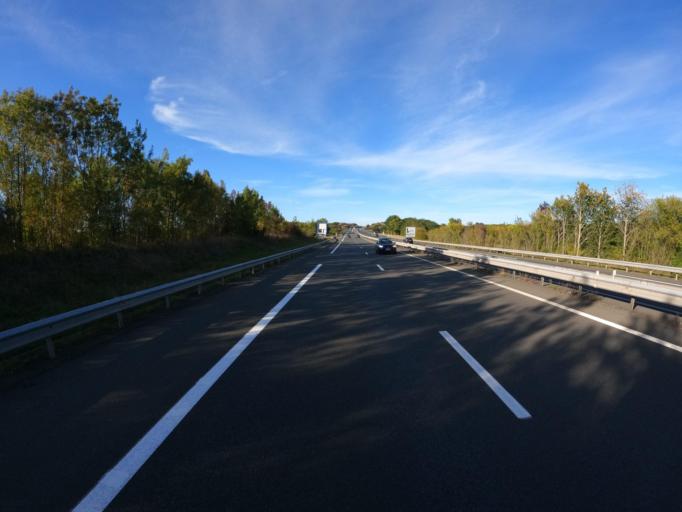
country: FR
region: Pays de la Loire
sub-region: Departement de Maine-et-Loire
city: Beaulieu-sur-Layon
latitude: 47.3067
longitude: -0.6075
